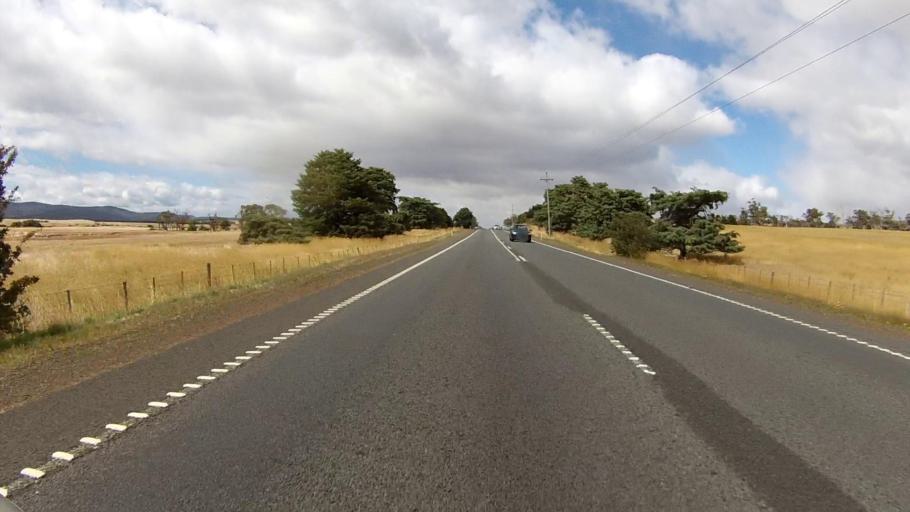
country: AU
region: Tasmania
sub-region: Northern Midlands
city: Evandale
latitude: -41.9514
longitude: 147.4951
